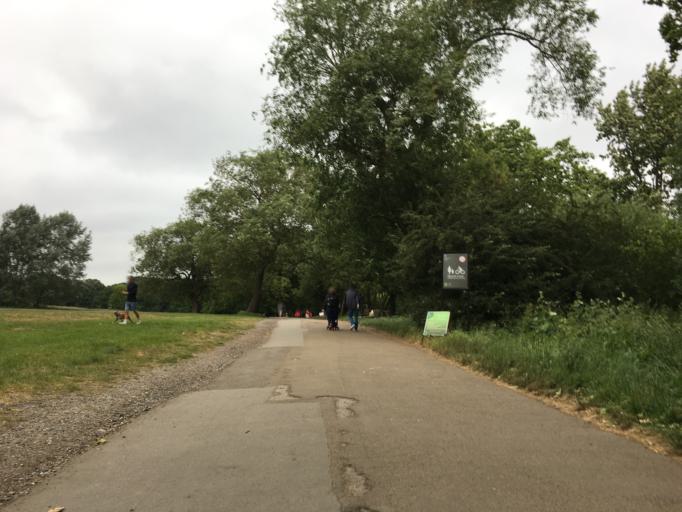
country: GB
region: England
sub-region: Greater London
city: Belsize Park
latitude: 51.5583
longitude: -0.1664
